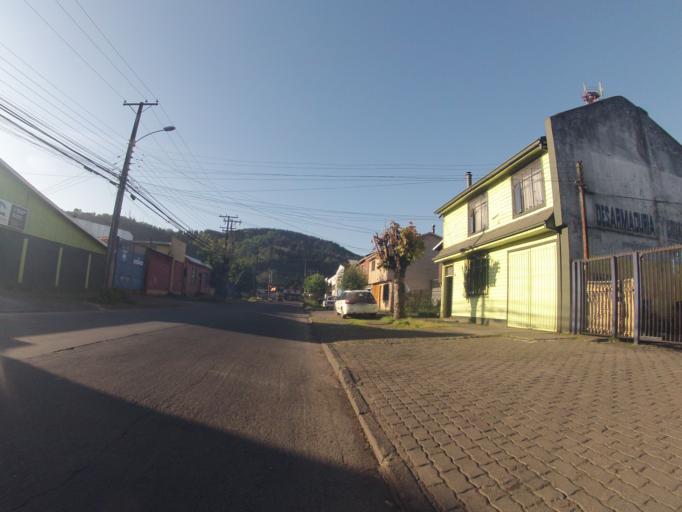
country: CL
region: Araucania
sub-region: Provincia de Cautin
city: Temuco
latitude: -38.7263
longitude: -72.5735
